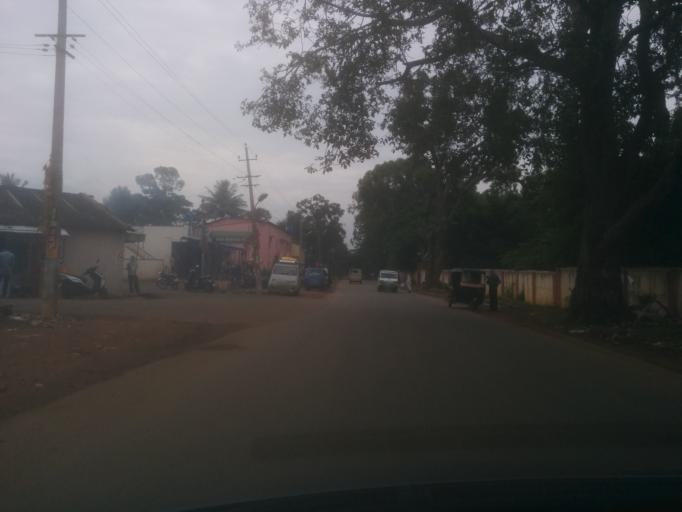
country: IN
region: Karnataka
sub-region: Chikmagalur
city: Chikmagalur
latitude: 13.3369
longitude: 75.7707
